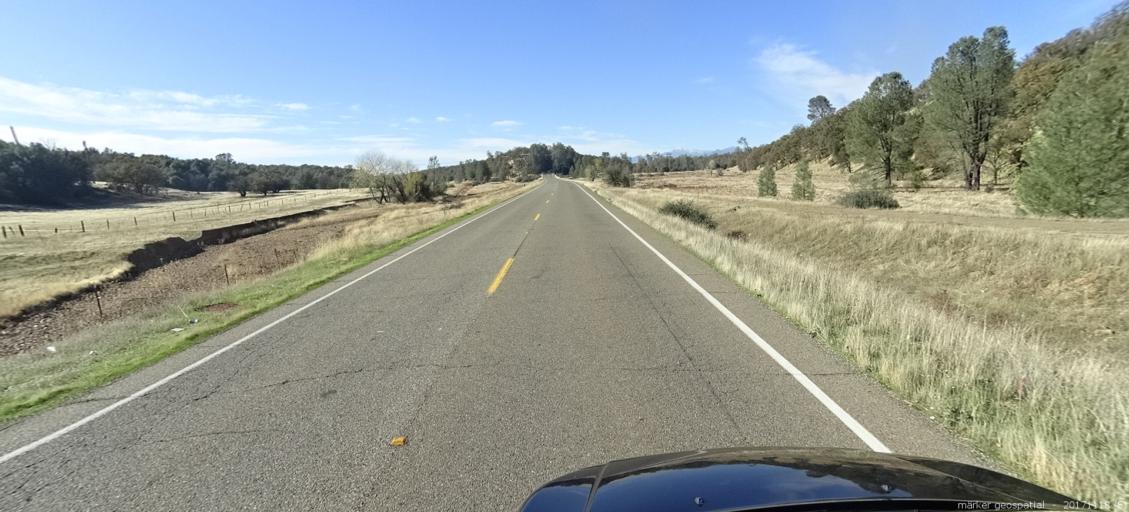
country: US
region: California
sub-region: Shasta County
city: Anderson
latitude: 40.4408
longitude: -122.3127
